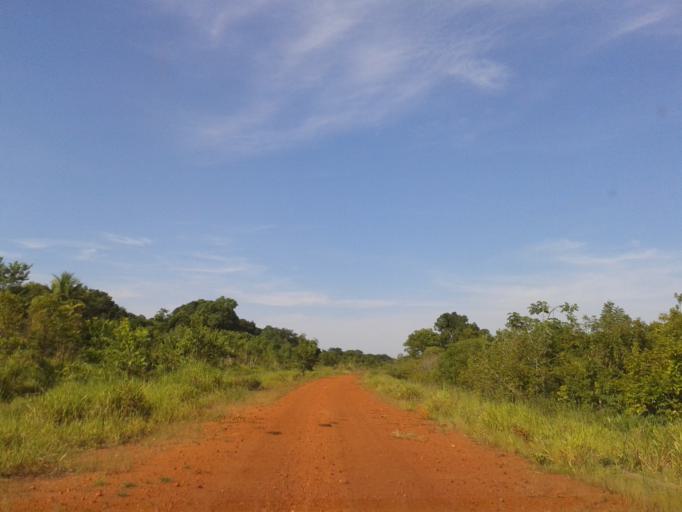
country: BR
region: Minas Gerais
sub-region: Santa Vitoria
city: Santa Vitoria
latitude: -19.1136
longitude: -50.5434
